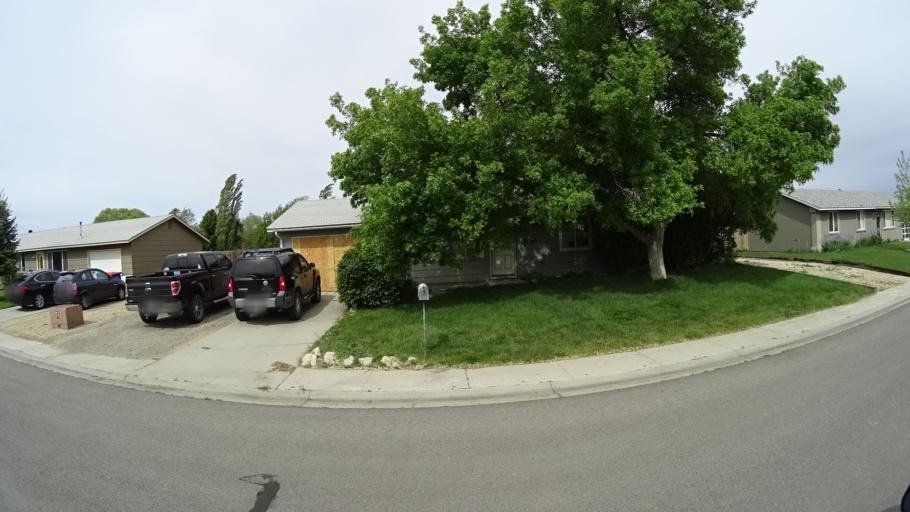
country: US
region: Idaho
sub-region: Ada County
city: Garden City
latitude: 43.5367
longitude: -116.3052
